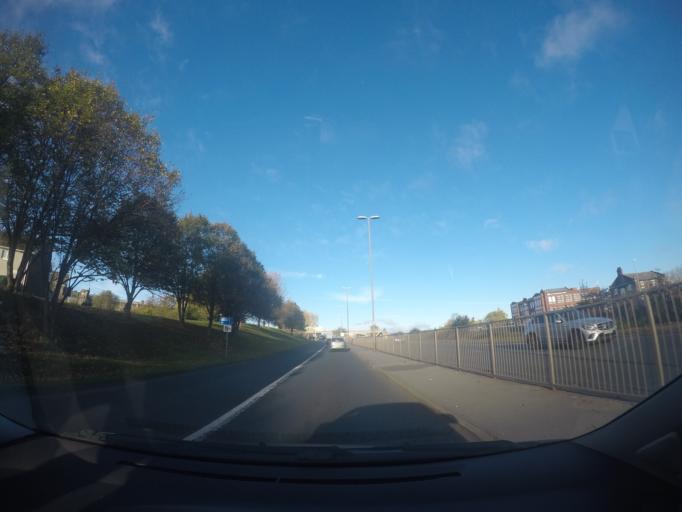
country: GB
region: England
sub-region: City and Borough of Leeds
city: Leeds
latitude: 53.7966
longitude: -1.5721
